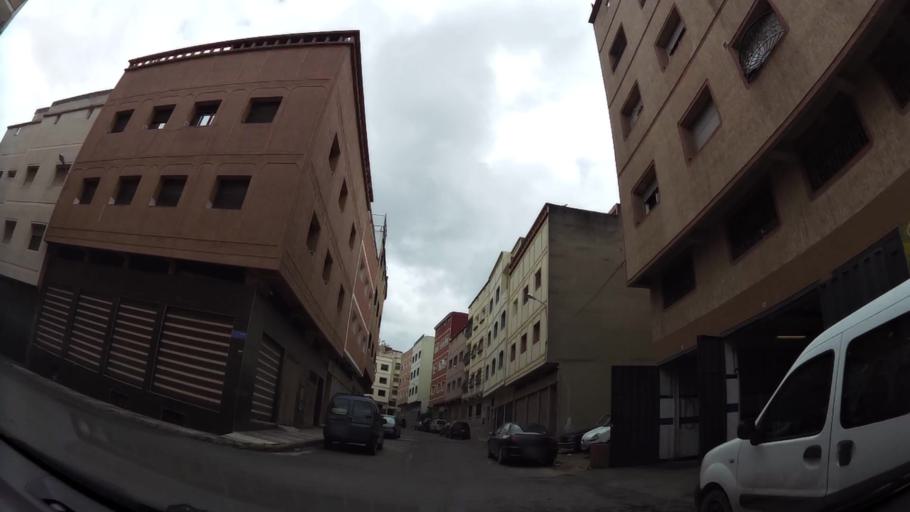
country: MA
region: Grand Casablanca
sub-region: Casablanca
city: Casablanca
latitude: 33.5328
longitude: -7.5908
